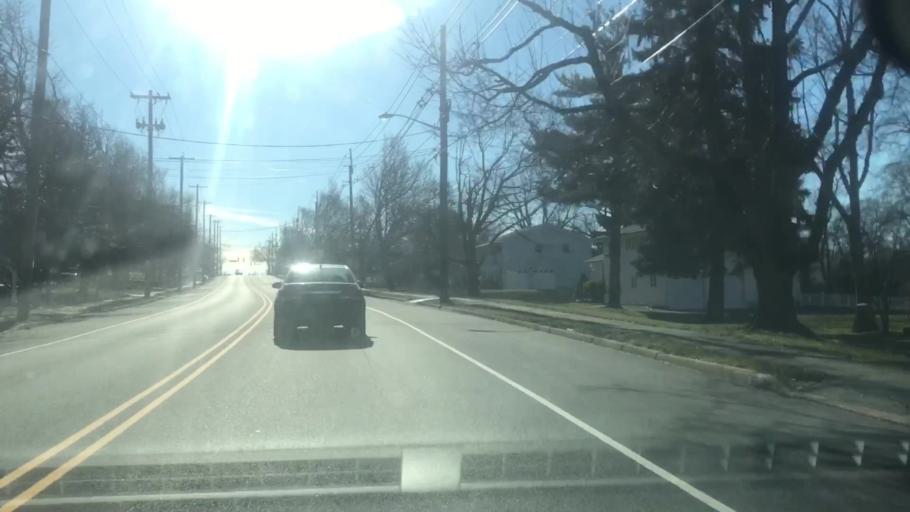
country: US
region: New Jersey
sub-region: Essex County
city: Livingston
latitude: 40.7996
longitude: -74.2970
